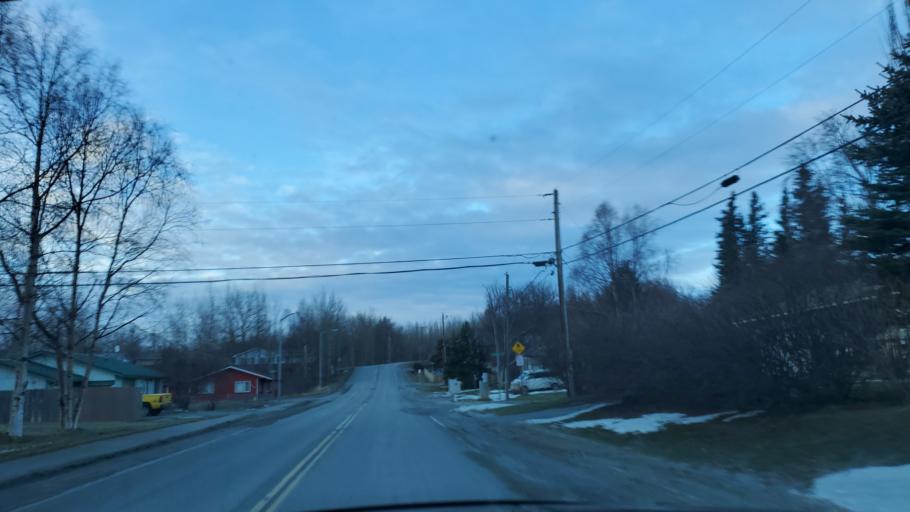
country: US
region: Alaska
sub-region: Matanuska-Susitna Borough
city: Palmer
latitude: 61.6139
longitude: -149.1149
